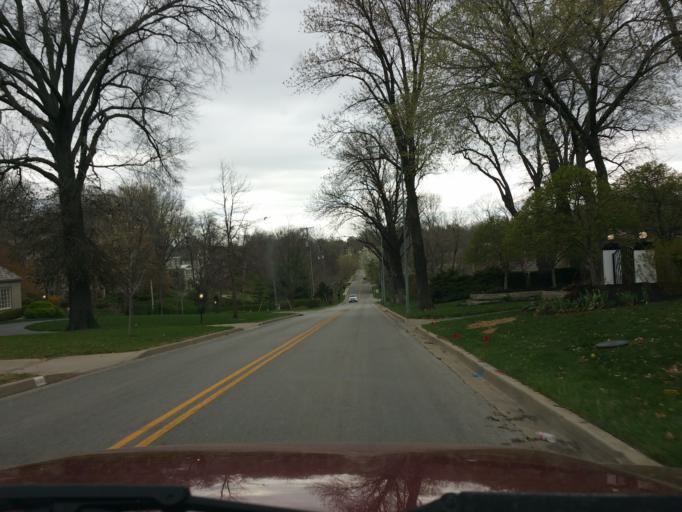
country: US
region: Kansas
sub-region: Johnson County
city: Mission Hills
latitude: 39.0101
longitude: -94.6078
